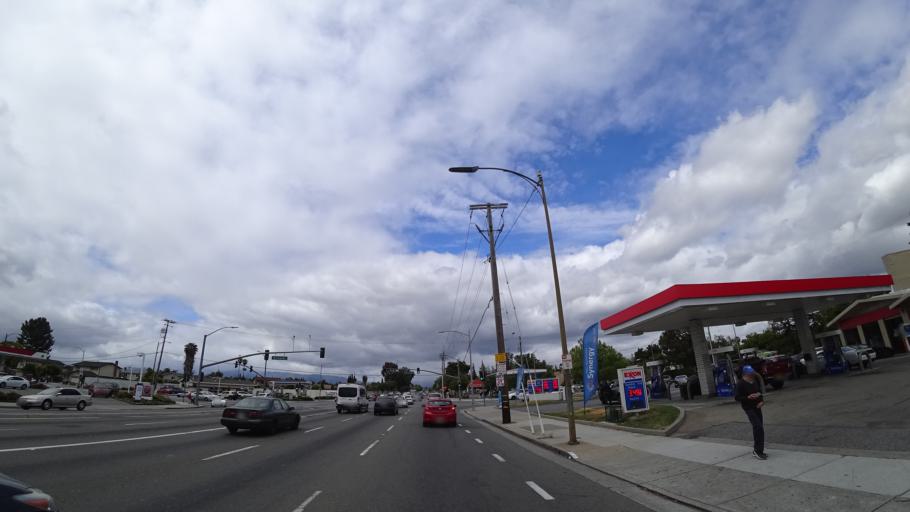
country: US
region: California
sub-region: Santa Clara County
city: Seven Trees
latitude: 37.3157
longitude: -121.8360
